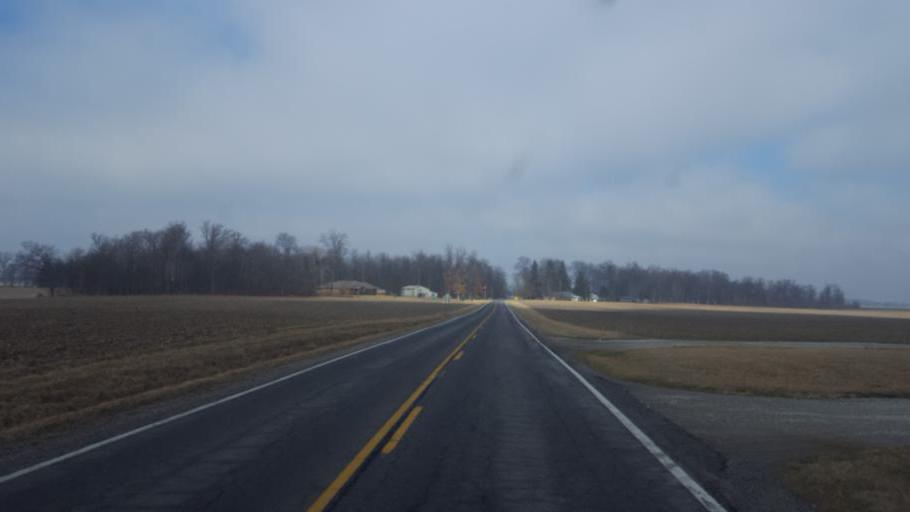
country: US
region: Ohio
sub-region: Crawford County
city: Bucyrus
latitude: 40.7629
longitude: -82.9177
